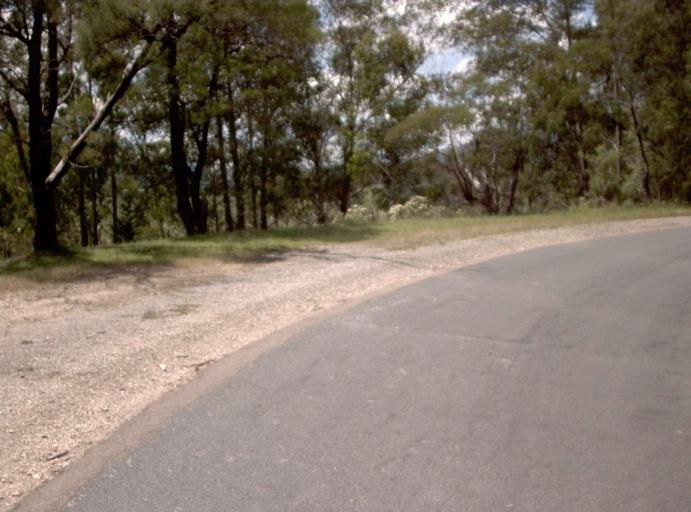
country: AU
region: New South Wales
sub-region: Bombala
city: Bombala
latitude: -37.4293
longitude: 149.0015
